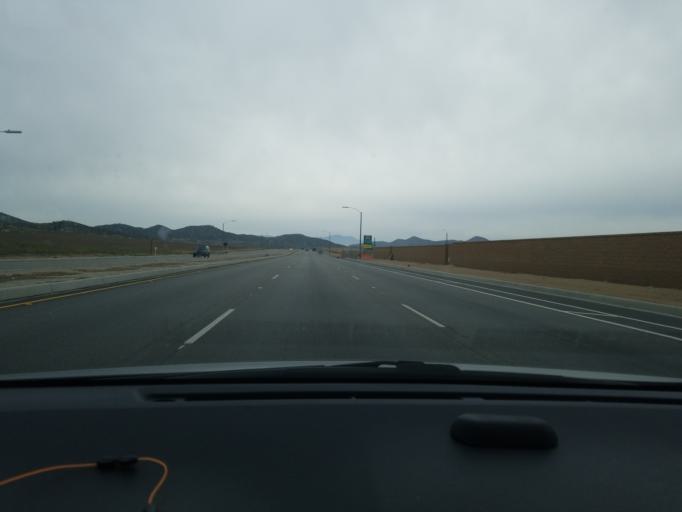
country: US
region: California
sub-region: Riverside County
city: Winchester
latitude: 33.6926
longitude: -117.1008
